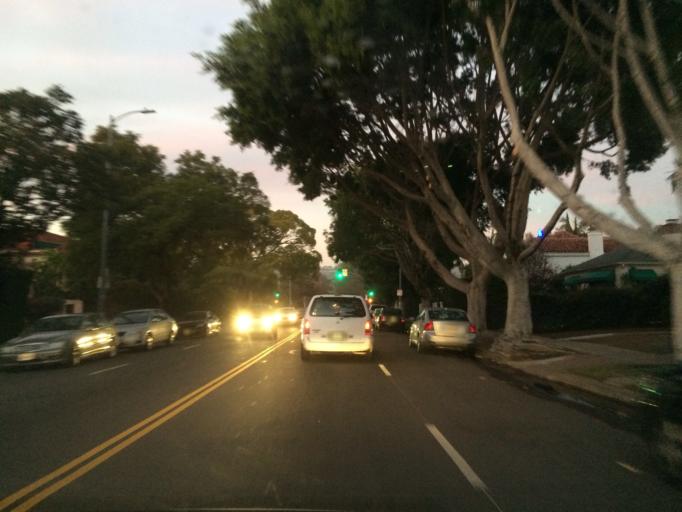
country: US
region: California
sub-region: Los Angeles County
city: West Hollywood
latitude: 34.0774
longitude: -118.3659
